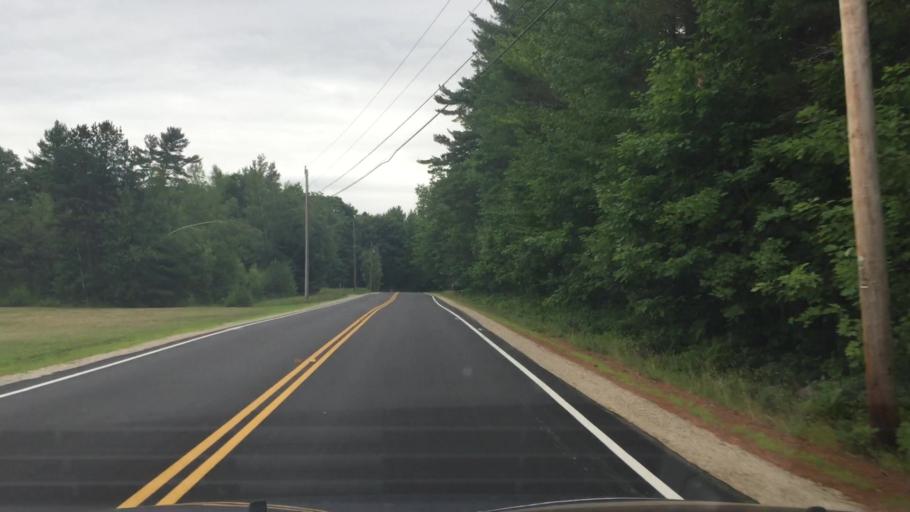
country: US
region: New Hampshire
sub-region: Carroll County
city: Freedom
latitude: 43.8206
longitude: -71.0681
